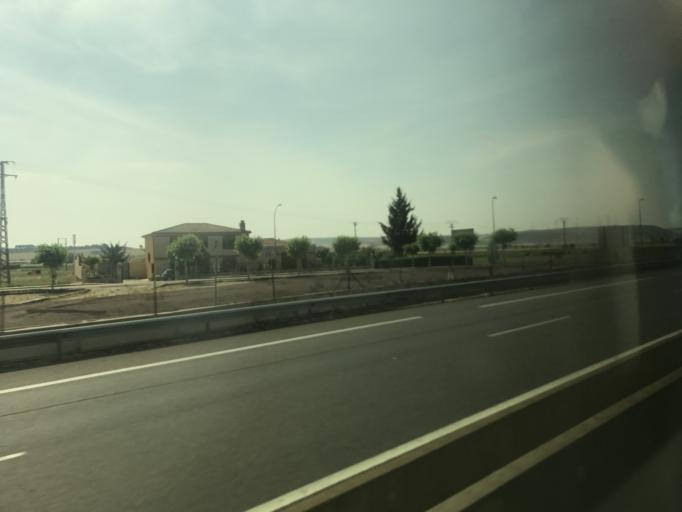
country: ES
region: Castille and Leon
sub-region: Provincia de Palencia
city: Quintana del Puente
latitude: 42.0823
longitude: -4.2099
